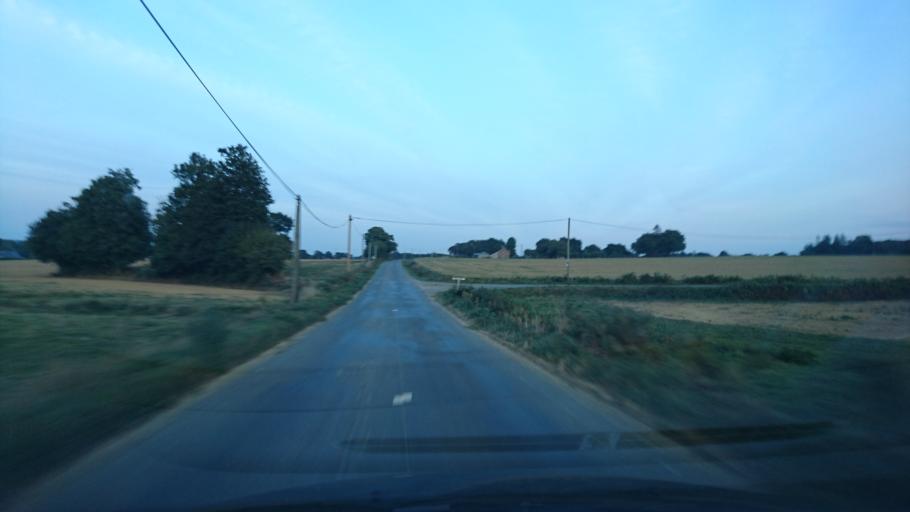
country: FR
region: Brittany
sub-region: Departement d'Ille-et-Vilaine
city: Guignen
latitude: 47.9113
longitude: -1.9058
